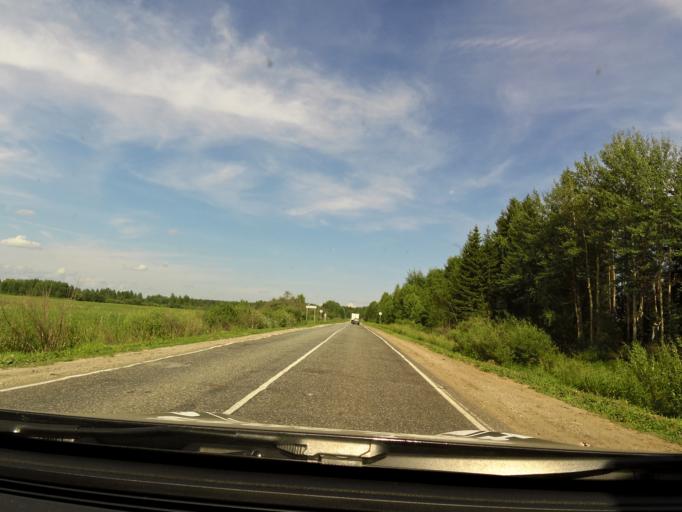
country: RU
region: Kirov
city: Slobodskoy
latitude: 58.7849
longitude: 50.4991
